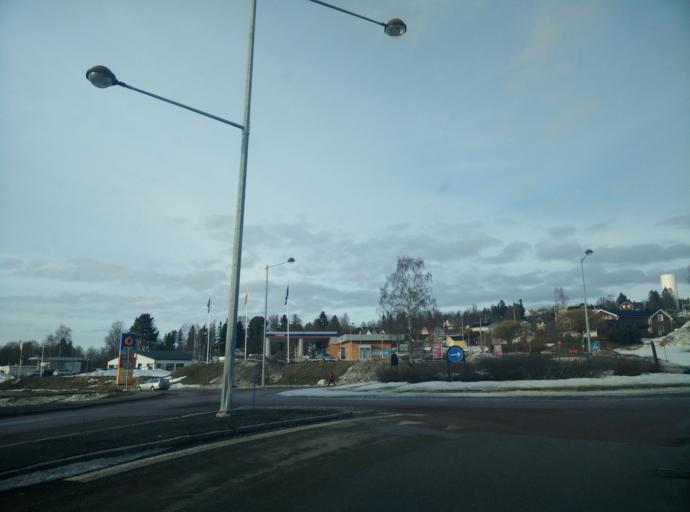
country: SE
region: Vaesternorrland
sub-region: Sundsvalls Kommun
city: Johannedal
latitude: 62.4312
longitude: 17.4157
